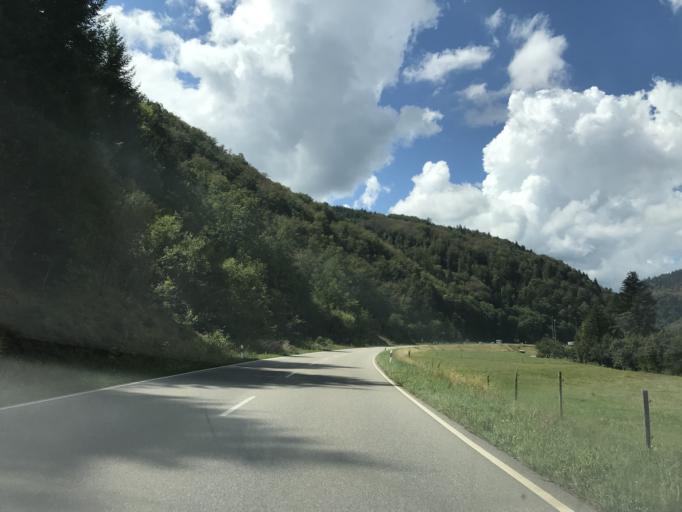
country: DE
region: Baden-Wuerttemberg
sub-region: Freiburg Region
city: Utzenfeld
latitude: 47.8004
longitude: 7.9224
